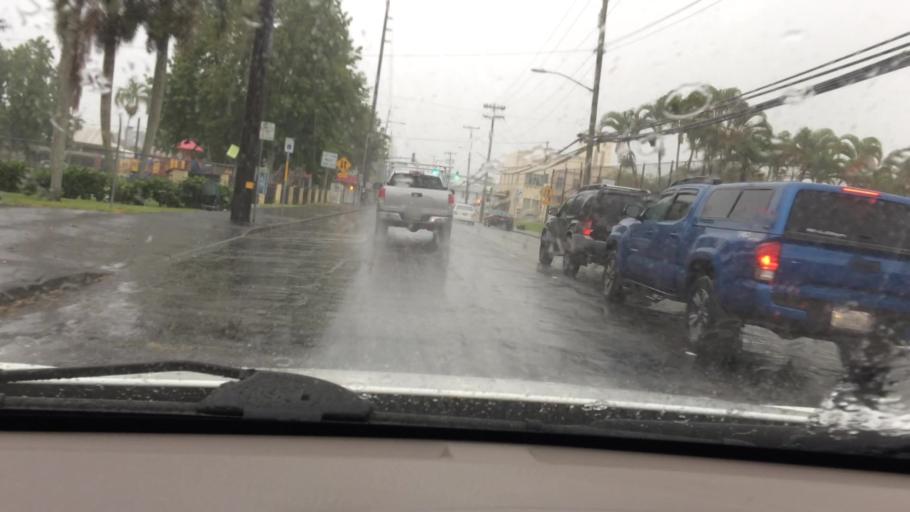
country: US
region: Hawaii
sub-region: Hawaii County
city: Hilo
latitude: 19.7215
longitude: -155.0867
